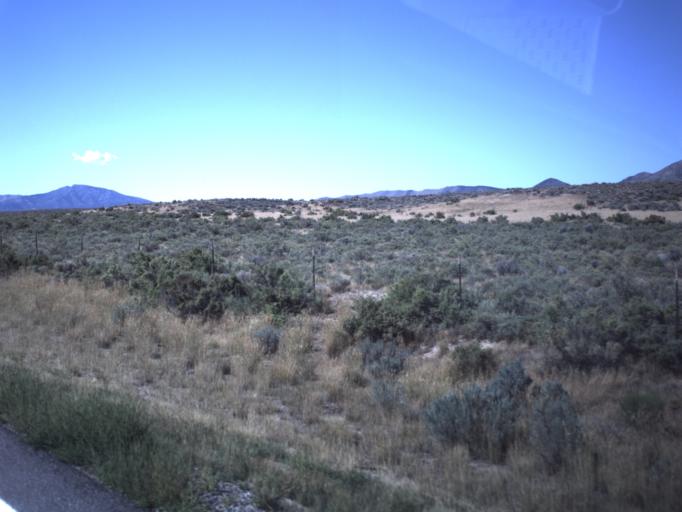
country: US
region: Utah
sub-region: Tooele County
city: Tooele
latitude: 40.1929
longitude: -112.4157
